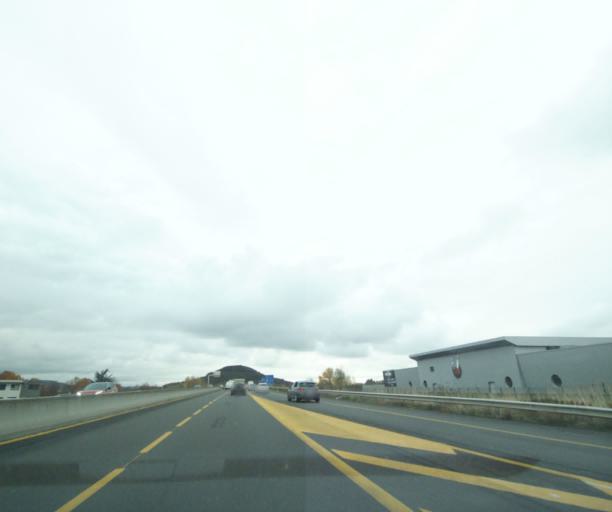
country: FR
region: Auvergne
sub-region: Departement du Puy-de-Dome
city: Perignat-les-Sarlieve
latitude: 45.7614
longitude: 3.1394
